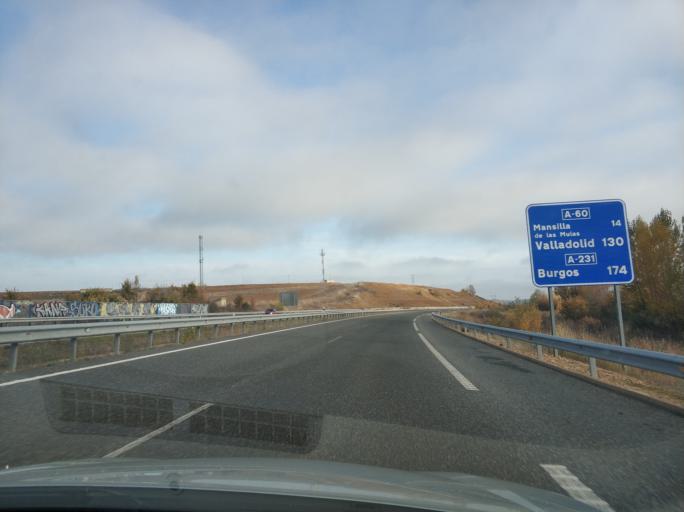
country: ES
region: Castille and Leon
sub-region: Provincia de Leon
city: Valdefresno
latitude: 42.5630
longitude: -5.4797
